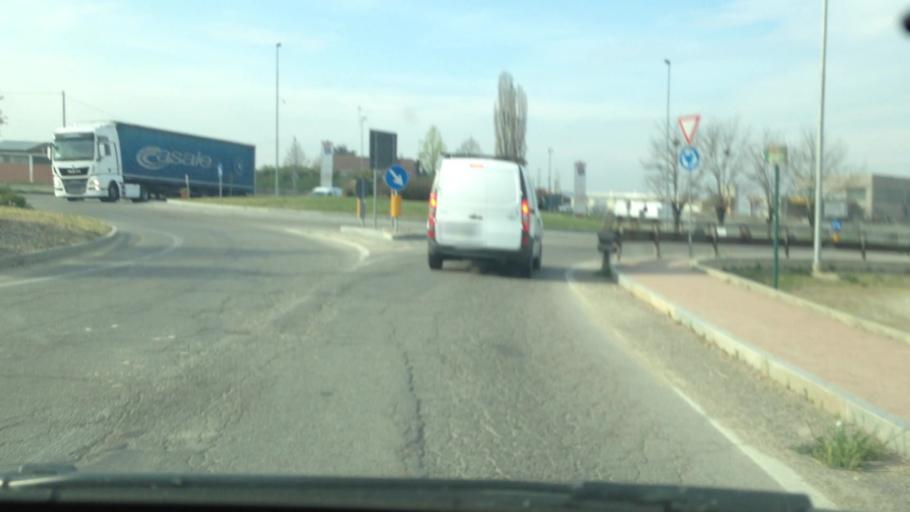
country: IT
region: Piedmont
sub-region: Provincia di Asti
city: San Damiano d'Asti
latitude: 44.8263
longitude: 8.0591
